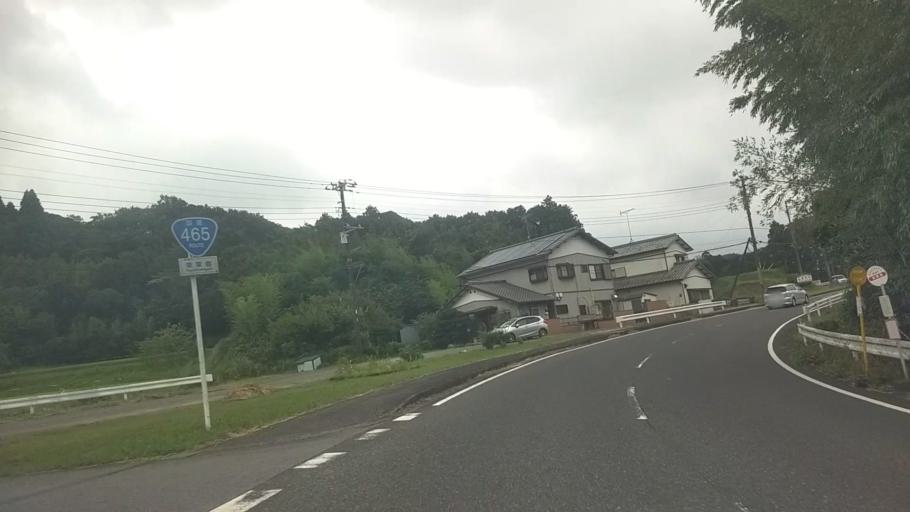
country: JP
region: Chiba
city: Kimitsu
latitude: 35.2474
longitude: 140.0040
